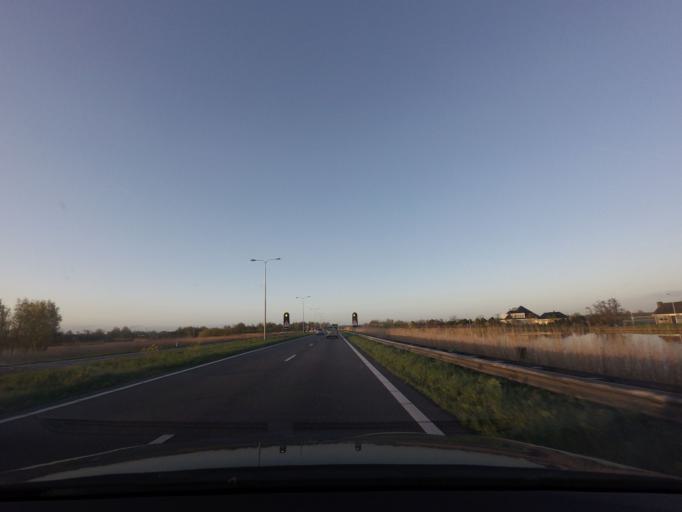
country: NL
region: North Holland
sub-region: Gemeente Zaanstad
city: Zaanstad
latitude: 52.4794
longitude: 4.7703
